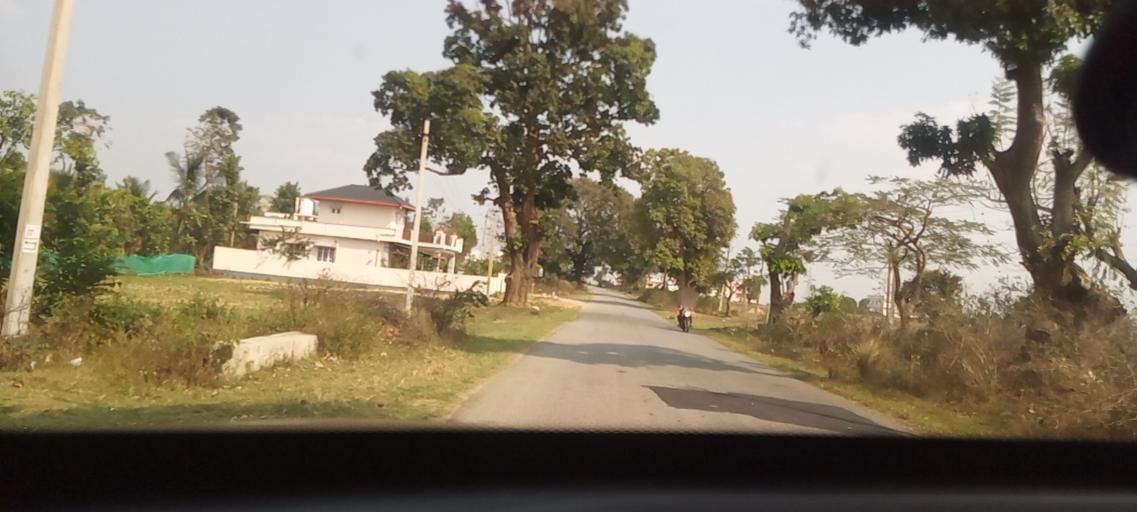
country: IN
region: Karnataka
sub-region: Hassan
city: Belur
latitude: 13.1755
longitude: 75.8508
